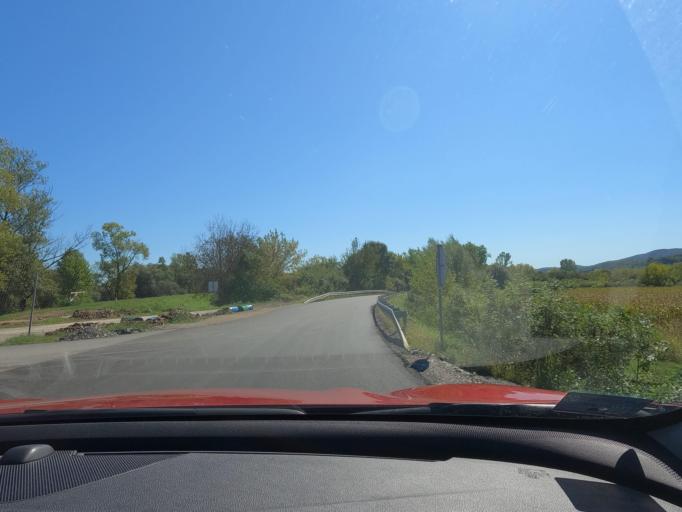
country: HR
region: Sisacko-Moslavacka
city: Petrinja
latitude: 45.4457
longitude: 16.2635
